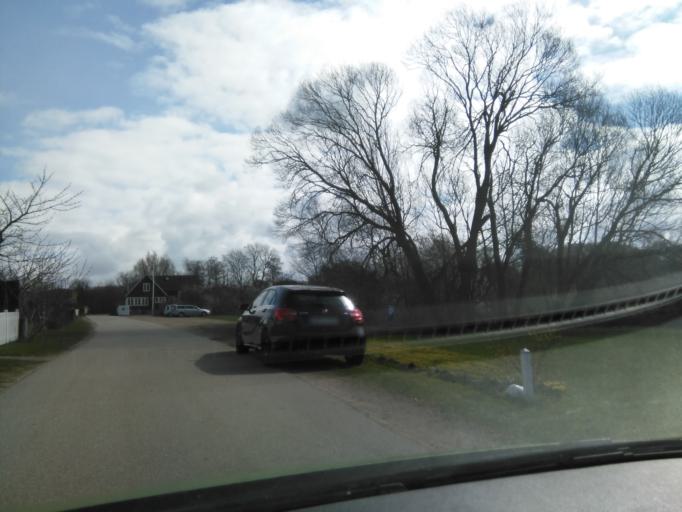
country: DK
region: South Denmark
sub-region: Middelfart Kommune
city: Strib
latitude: 55.5422
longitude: 9.7803
